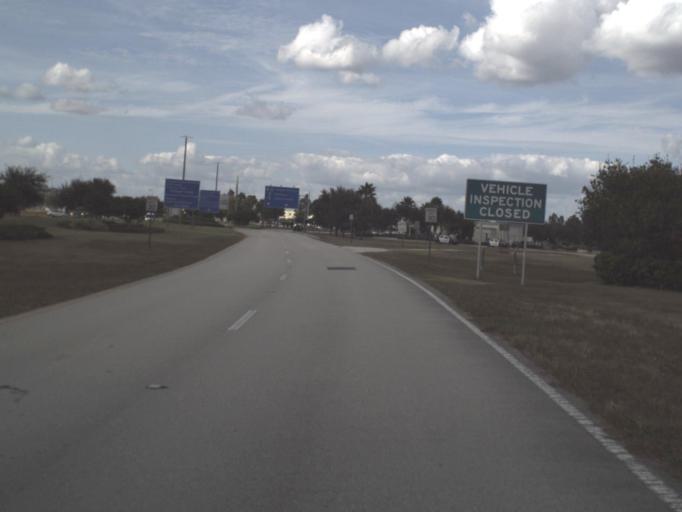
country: US
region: Florida
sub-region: Seminole County
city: Midway
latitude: 28.7711
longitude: -81.2385
